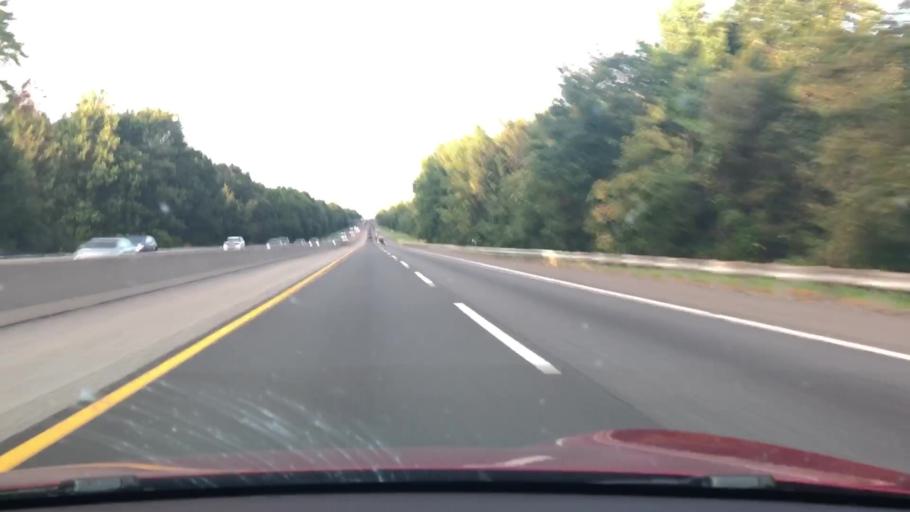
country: US
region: New Jersey
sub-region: Gloucester County
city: Mullica Hill
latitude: 39.7748
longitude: -75.2399
